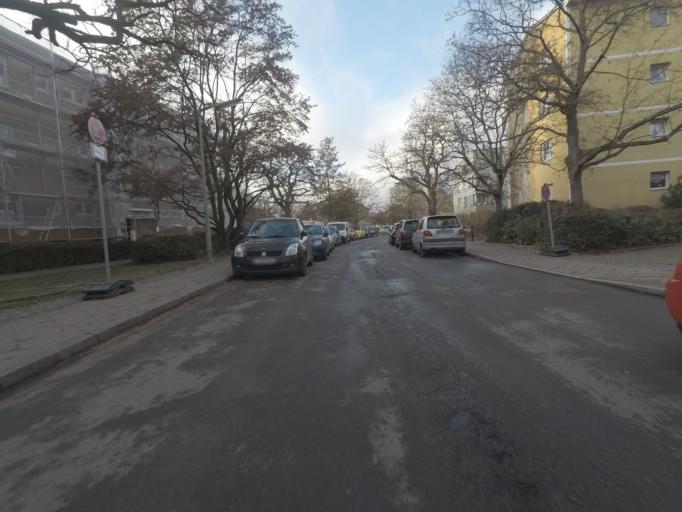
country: DE
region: Berlin
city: Marienfelde
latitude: 52.4128
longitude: 13.3456
